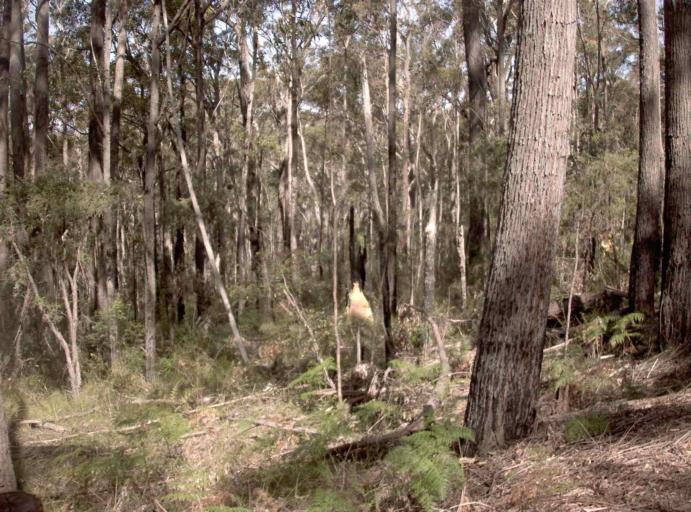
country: AU
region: New South Wales
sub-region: Bega Valley
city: Eden
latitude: -37.5405
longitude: 149.6970
